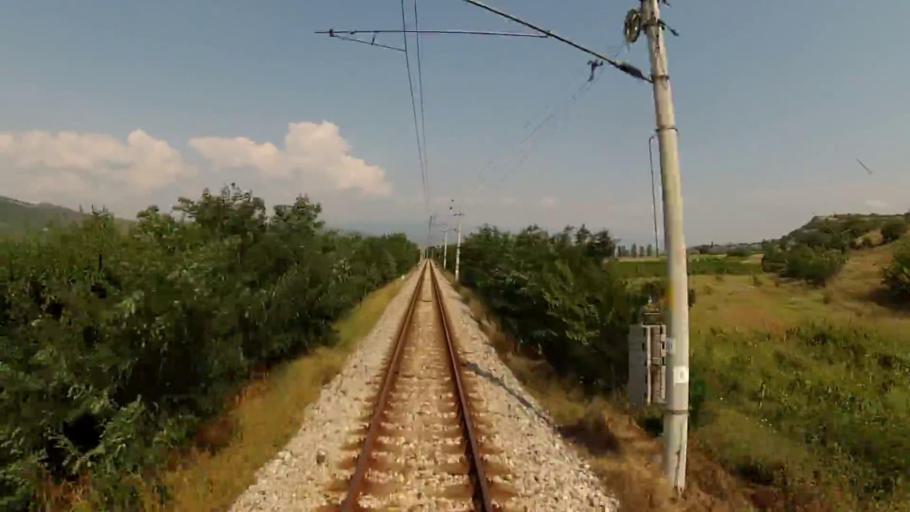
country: BG
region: Blagoevgrad
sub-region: Obshtina Strumyani
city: Strumyani
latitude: 41.5953
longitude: 23.2306
